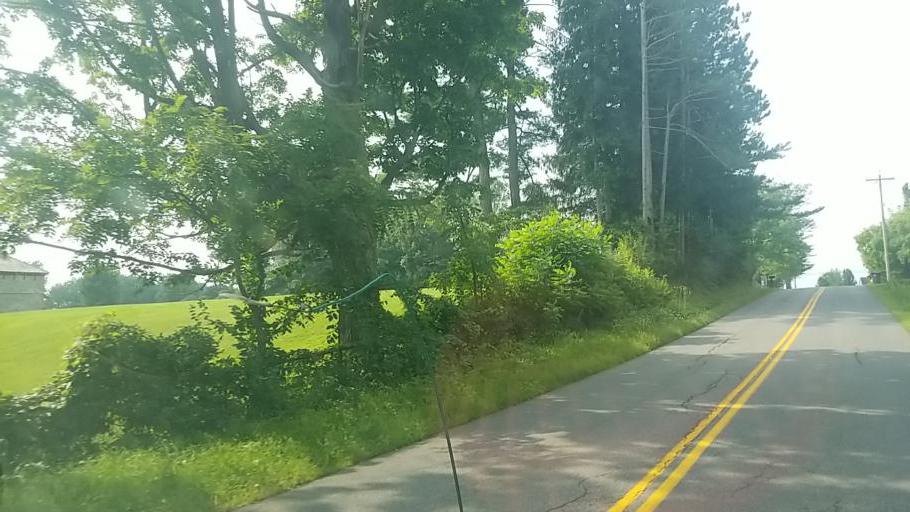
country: US
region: New York
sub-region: Fulton County
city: Johnstown
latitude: 43.0170
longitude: -74.3842
